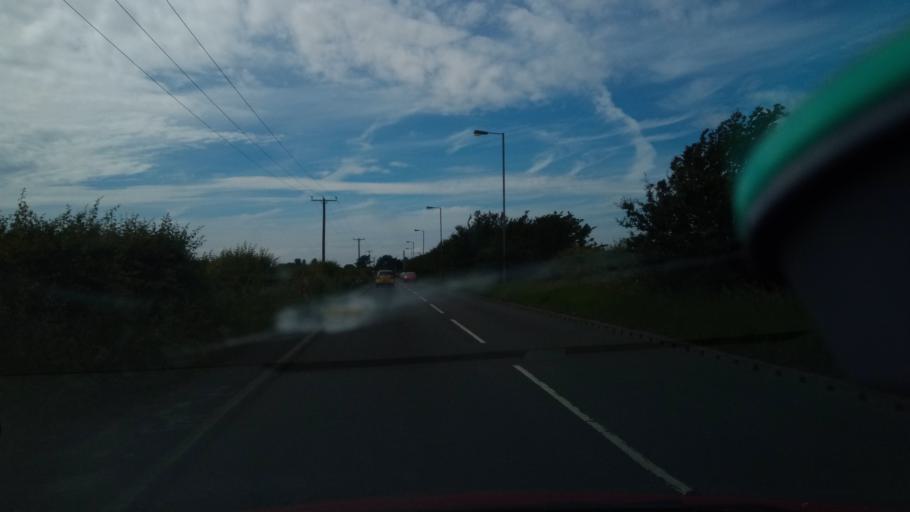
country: GB
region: England
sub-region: Sefton
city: Formby
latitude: 53.5450
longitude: -3.0510
